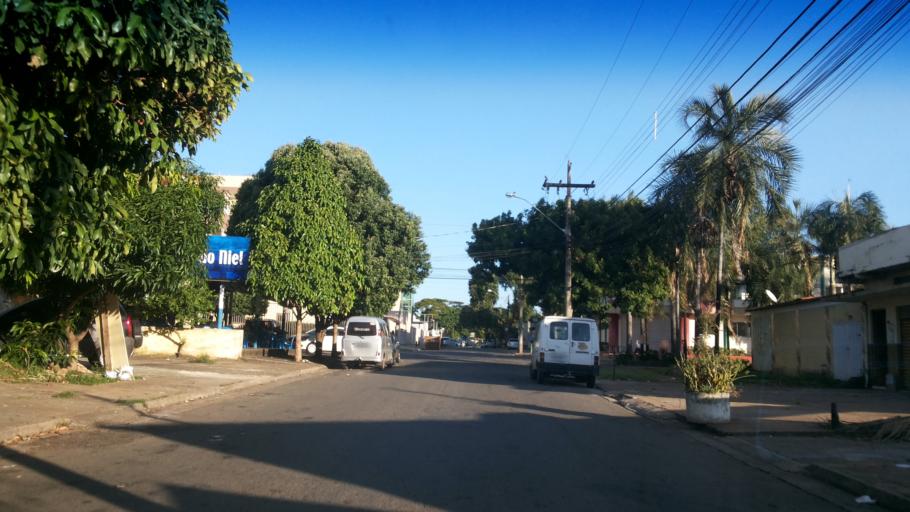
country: BR
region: Goias
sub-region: Goiania
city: Goiania
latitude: -16.6532
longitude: -49.2715
